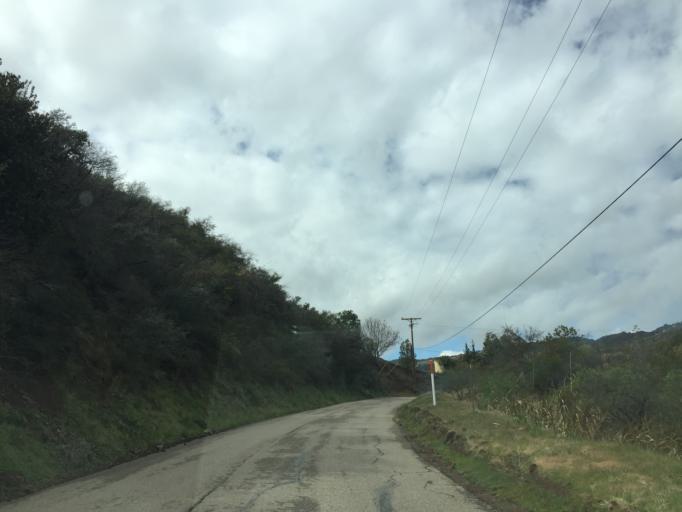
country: US
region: California
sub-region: Santa Barbara County
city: Goleta
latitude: 34.4791
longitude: -119.7969
